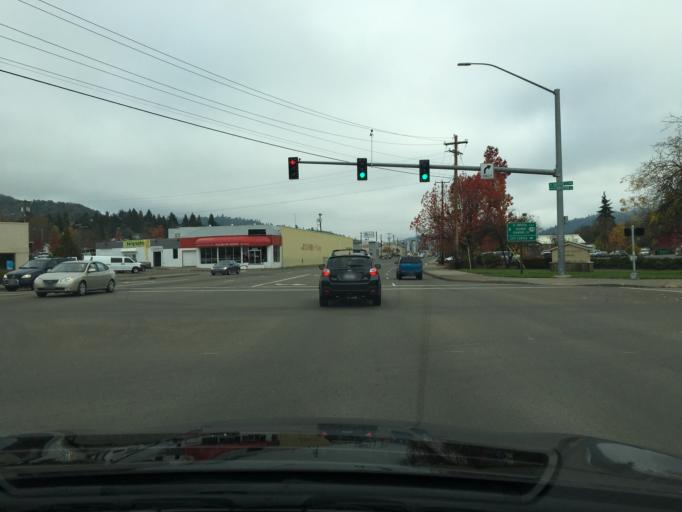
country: US
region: Oregon
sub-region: Douglas County
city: Roseburg
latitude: 43.2135
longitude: -123.3414
